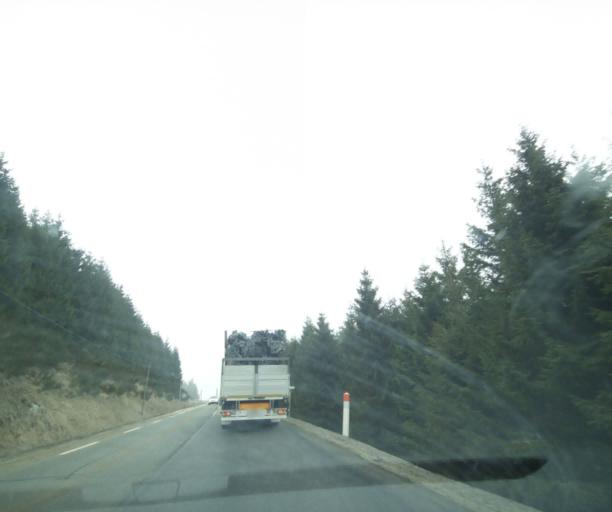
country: FR
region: Languedoc-Roussillon
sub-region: Departement de la Lozere
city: Langogne
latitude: 44.7063
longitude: 4.0086
